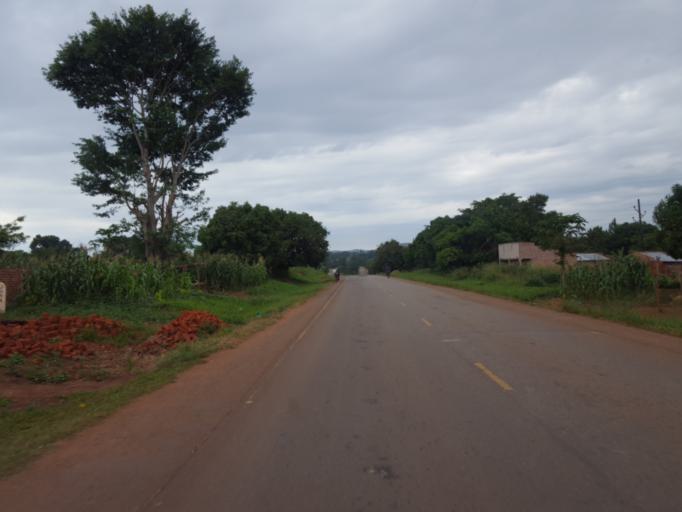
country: UG
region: Central Region
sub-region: Kiboga District
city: Kiboga
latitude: 1.0229
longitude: 31.6846
